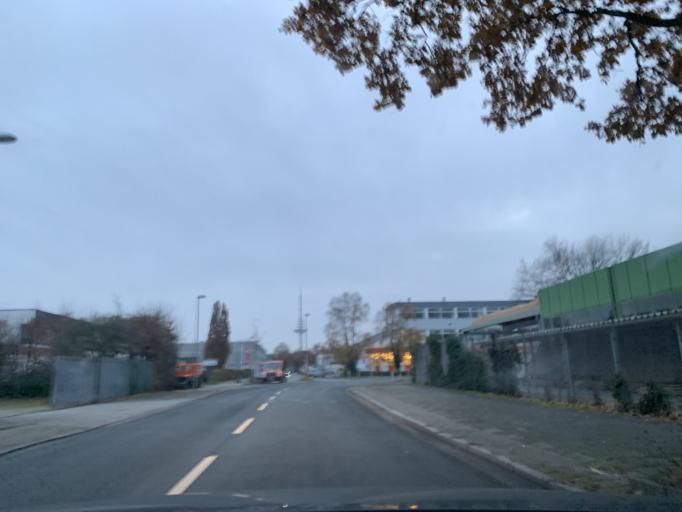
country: DE
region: Bremen
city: Bremen
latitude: 53.1078
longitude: 8.8004
